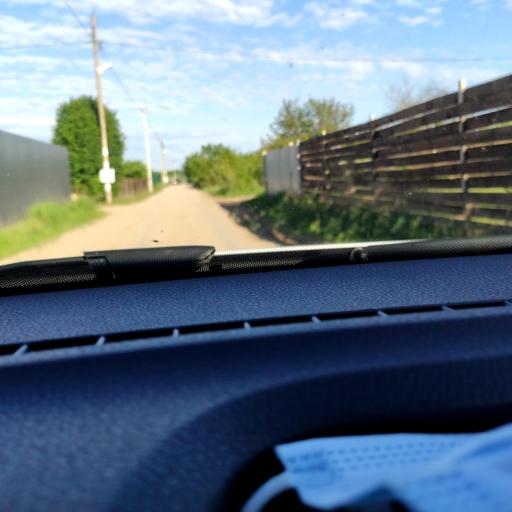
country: RU
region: Voronezj
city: Ramon'
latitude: 51.9455
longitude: 39.3549
